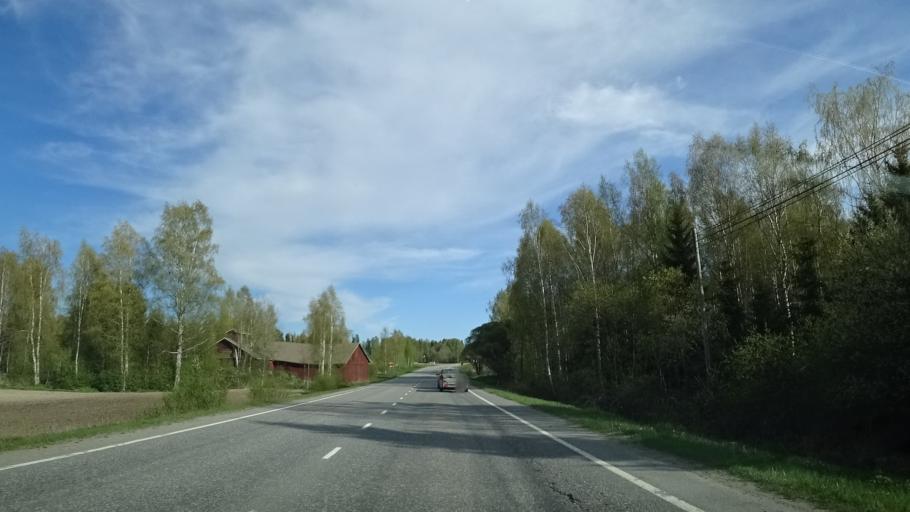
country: FI
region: Haeme
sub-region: Riihimaeki
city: Loppi
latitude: 60.6132
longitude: 24.4694
